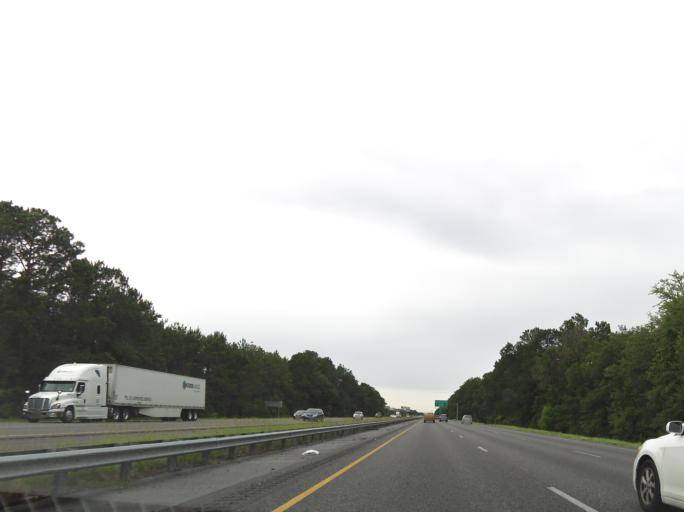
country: US
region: Georgia
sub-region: Lowndes County
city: Valdosta
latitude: 30.7604
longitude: -83.2812
